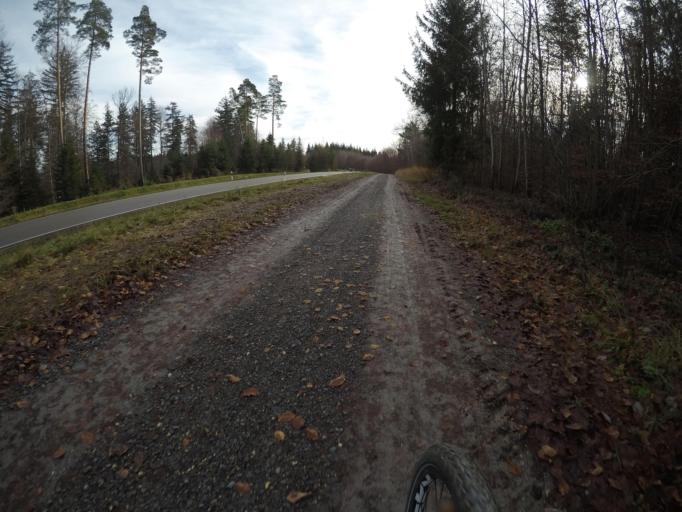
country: DE
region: Baden-Wuerttemberg
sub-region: Regierungsbezirk Stuttgart
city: Winterbach
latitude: 48.7698
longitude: 9.4758
